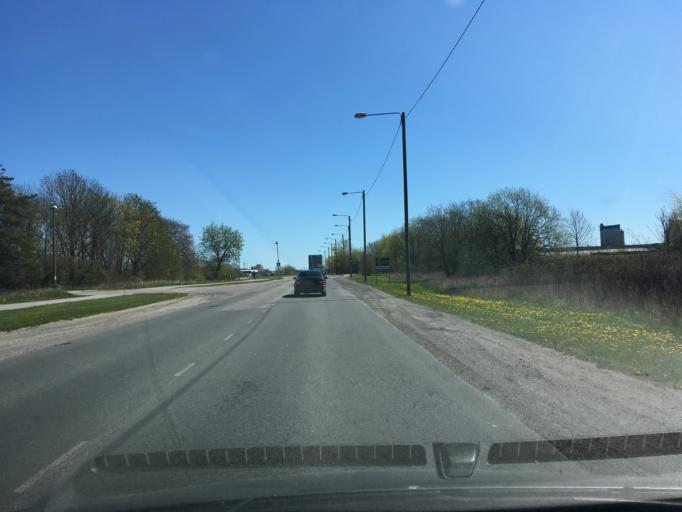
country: EE
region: Harju
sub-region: Joelaehtme vald
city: Loo
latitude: 59.4603
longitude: 24.9262
